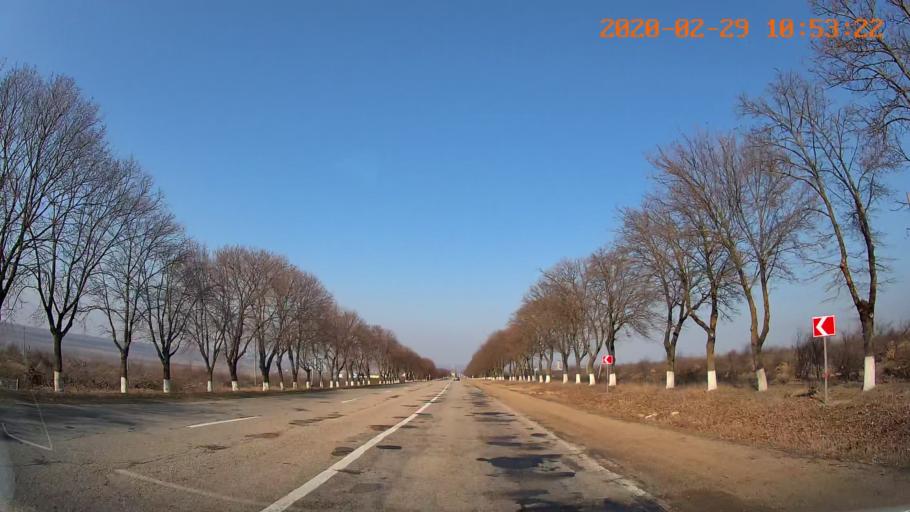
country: MD
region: Telenesti
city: Grigoriopol
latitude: 47.1152
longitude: 29.3371
